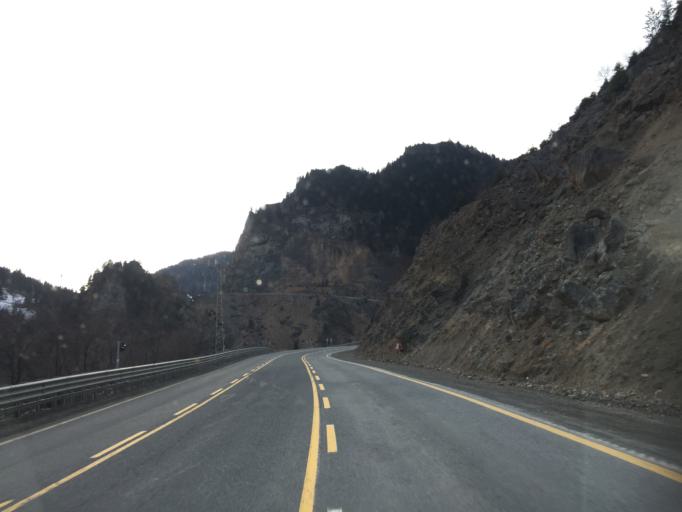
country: TR
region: Gumushane
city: Yaglidere
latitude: 40.6991
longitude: 39.4725
